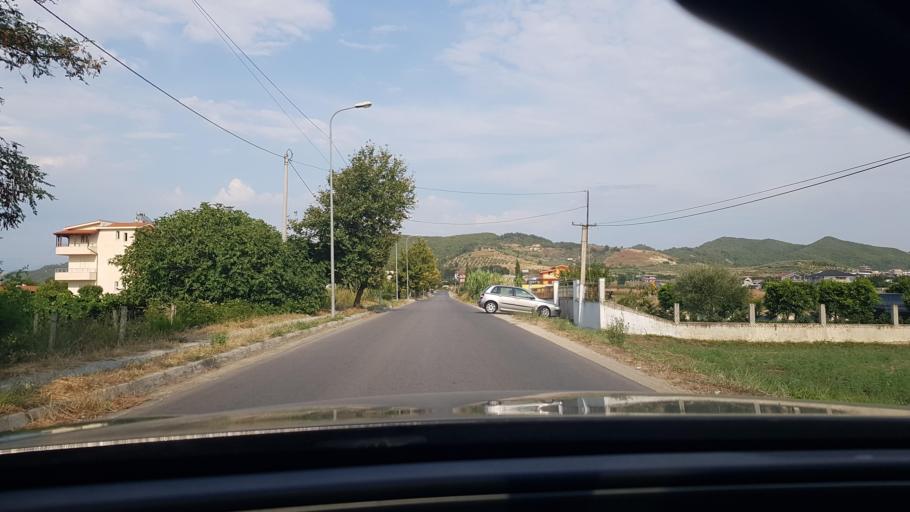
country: AL
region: Durres
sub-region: Rrethi i Durresit
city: Manze
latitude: 41.4745
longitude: 19.5574
